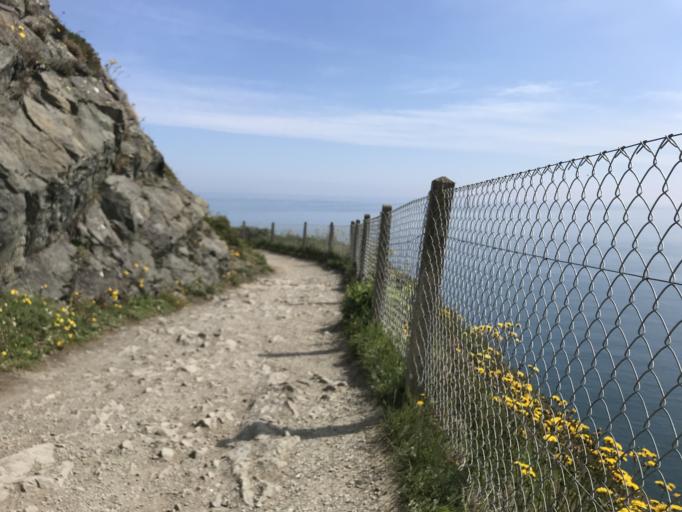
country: IE
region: Leinster
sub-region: Wicklow
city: Bray
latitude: 53.1873
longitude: -6.0776
